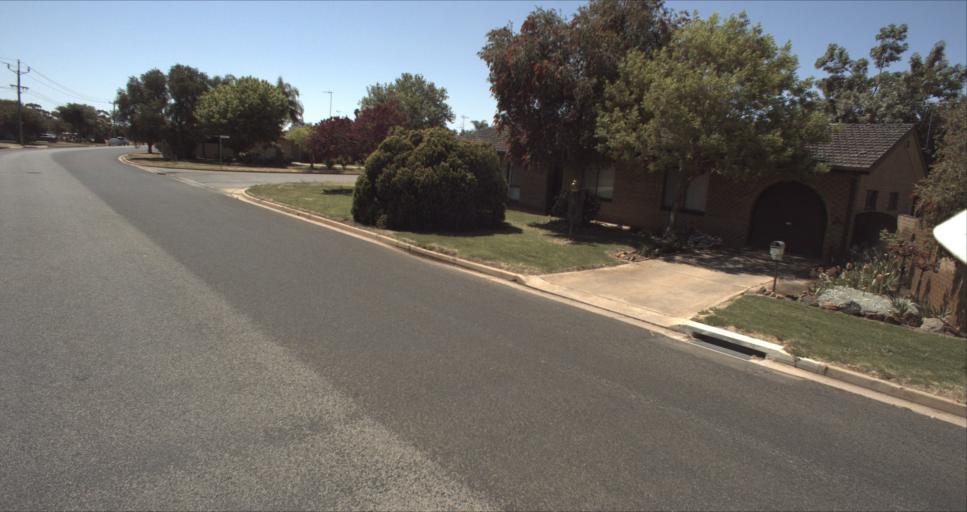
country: AU
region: New South Wales
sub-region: Leeton
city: Leeton
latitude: -34.5462
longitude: 146.4002
